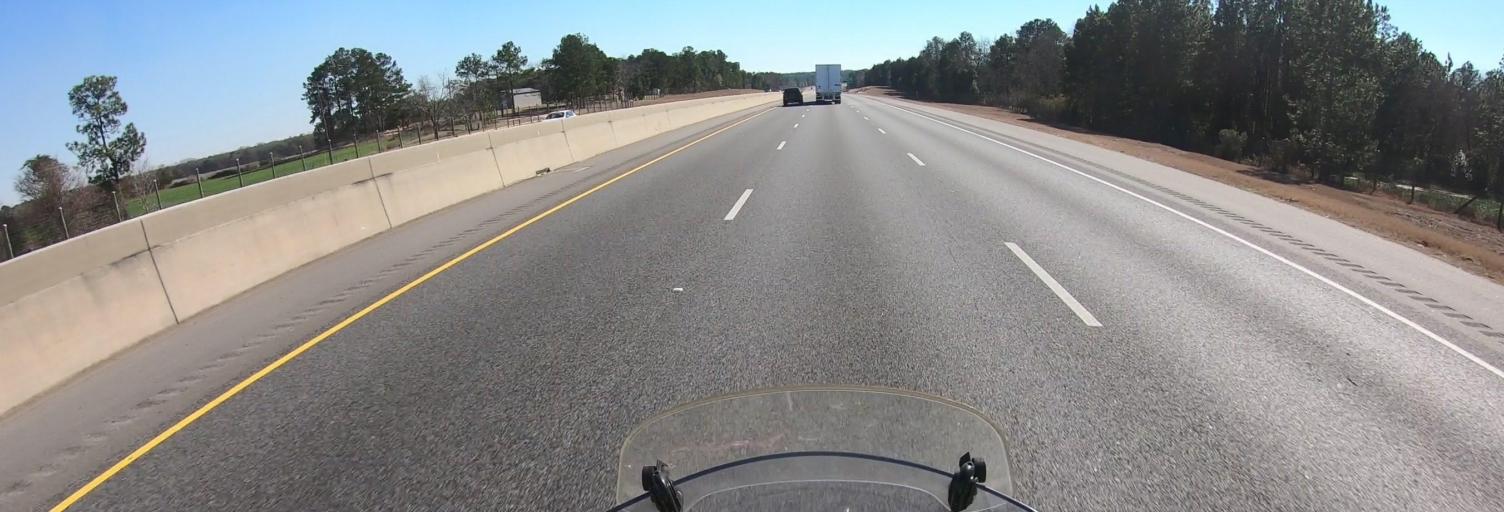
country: US
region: Georgia
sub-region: Tift County
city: Tifton
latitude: 31.5260
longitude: -83.5217
